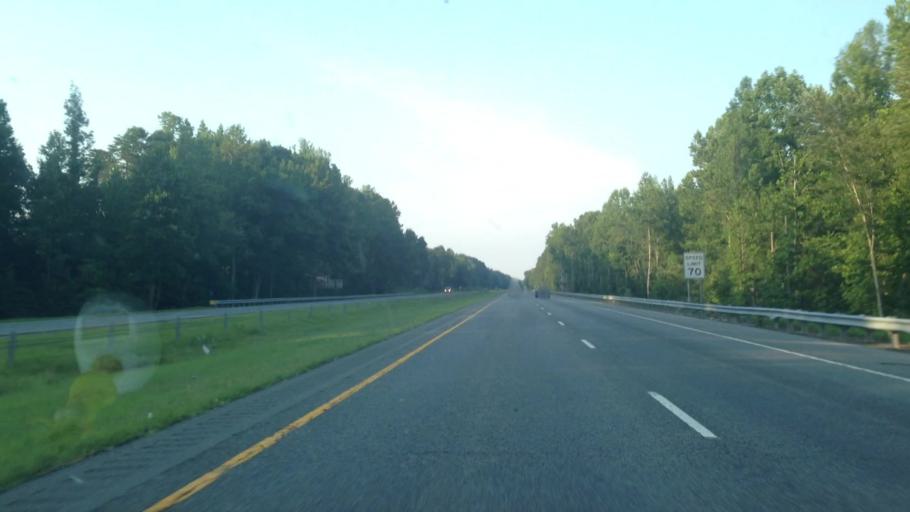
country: US
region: North Carolina
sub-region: Rockingham County
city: Reidsville
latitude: 36.4088
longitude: -79.5933
